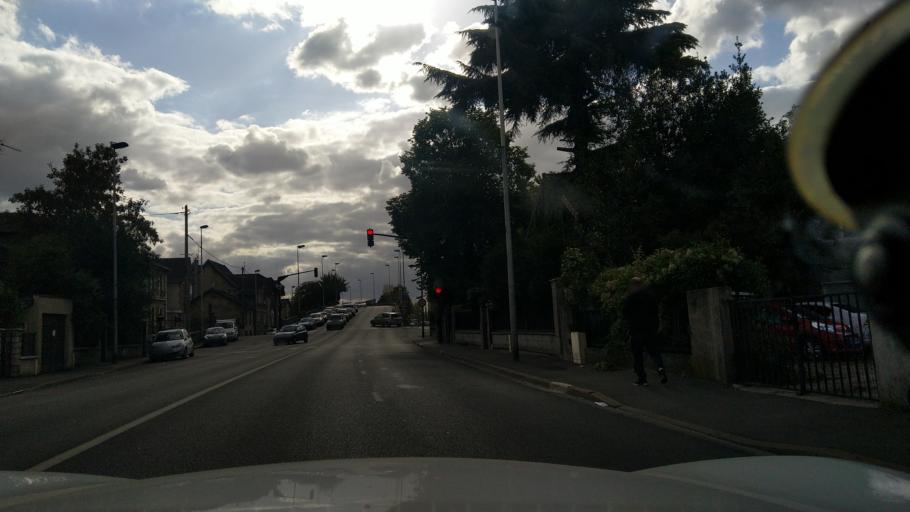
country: FR
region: Ile-de-France
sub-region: Departement de Seine-Saint-Denis
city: Aulnay-sous-Bois
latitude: 48.9332
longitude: 2.4894
